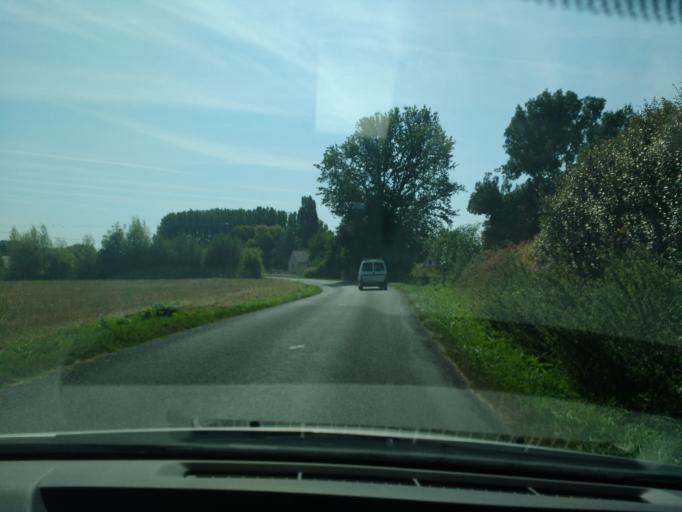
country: FR
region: Pays de la Loire
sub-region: Departement de Maine-et-Loire
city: Beaufort-en-Vallee
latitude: 47.4916
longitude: -0.2035
